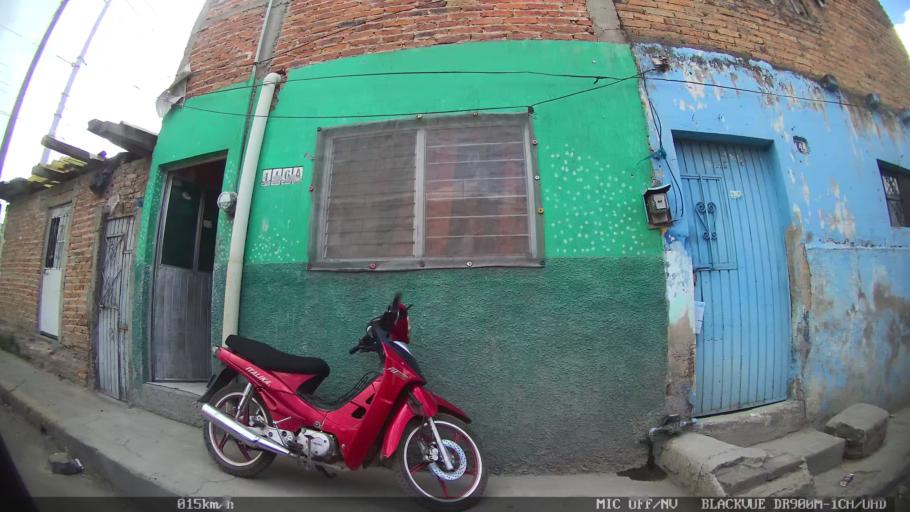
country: MX
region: Jalisco
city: Tlaquepaque
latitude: 20.6590
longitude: -103.2625
